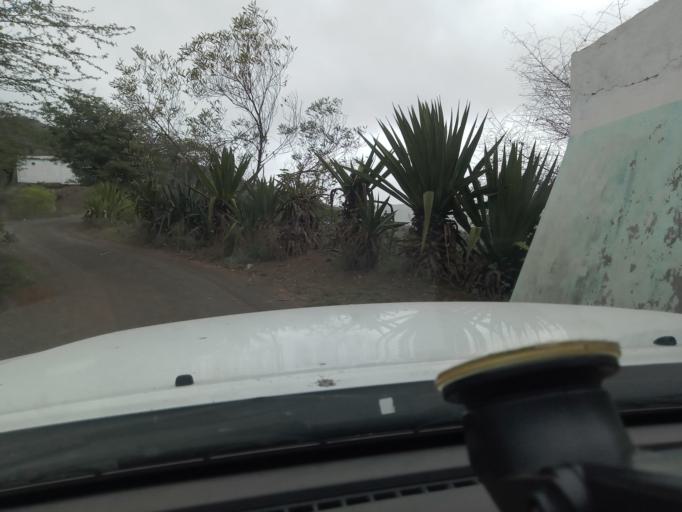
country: CV
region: Santa Catarina
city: Assomada
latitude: 15.1397
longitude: -23.6427
